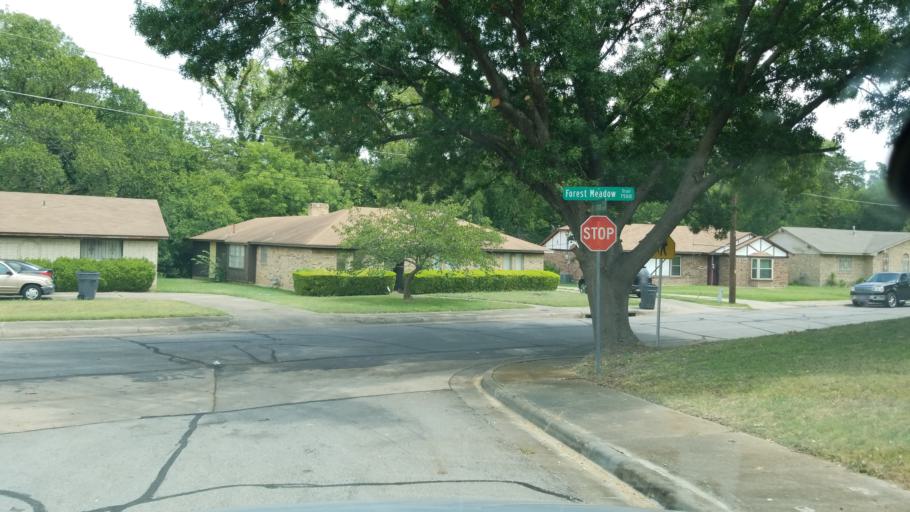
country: US
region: Texas
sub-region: Dallas County
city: Duncanville
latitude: 32.6578
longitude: -96.8471
